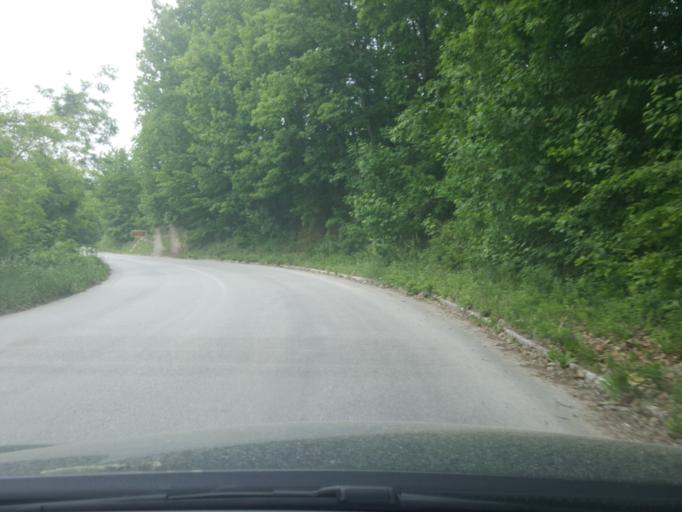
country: RS
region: Central Serbia
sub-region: Zlatiborski Okrug
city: Bajina Basta
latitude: 43.9467
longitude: 19.5551
